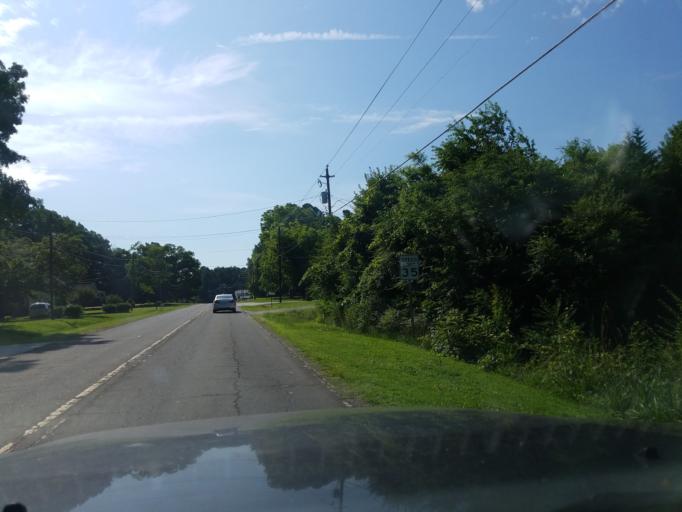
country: US
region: North Carolina
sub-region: Granville County
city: Oxford
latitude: 36.3164
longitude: -78.5732
